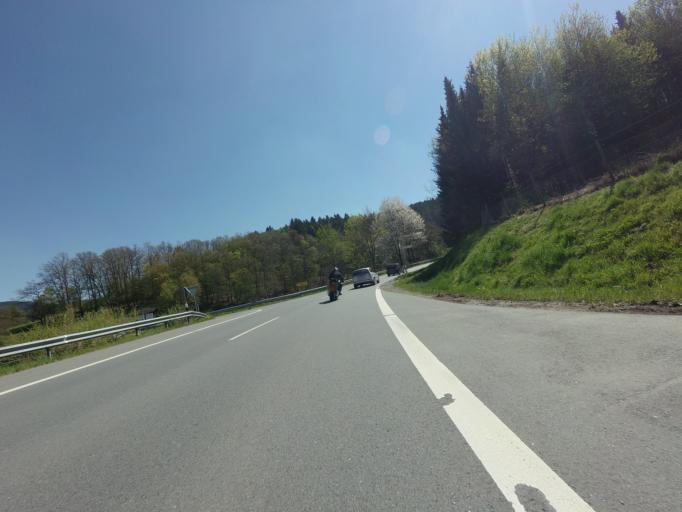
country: DE
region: North Rhine-Westphalia
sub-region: Regierungsbezirk Arnsberg
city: Kirchhundem
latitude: 51.0892
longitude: 8.1421
